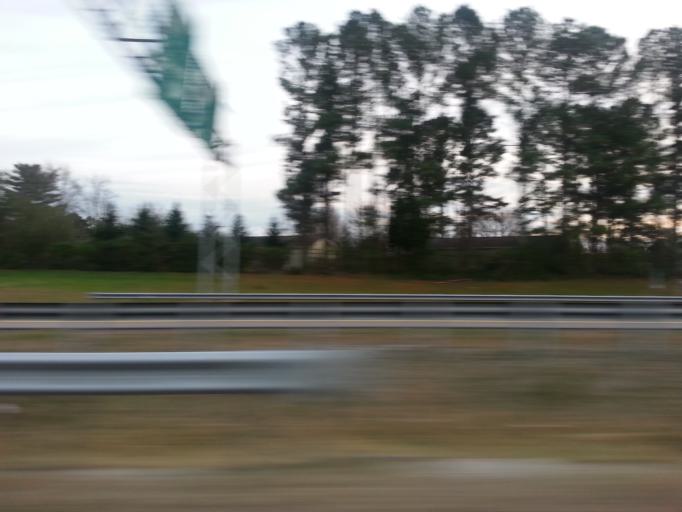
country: US
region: Tennessee
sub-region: Monroe County
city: Madisonville
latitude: 35.5086
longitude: -84.3742
